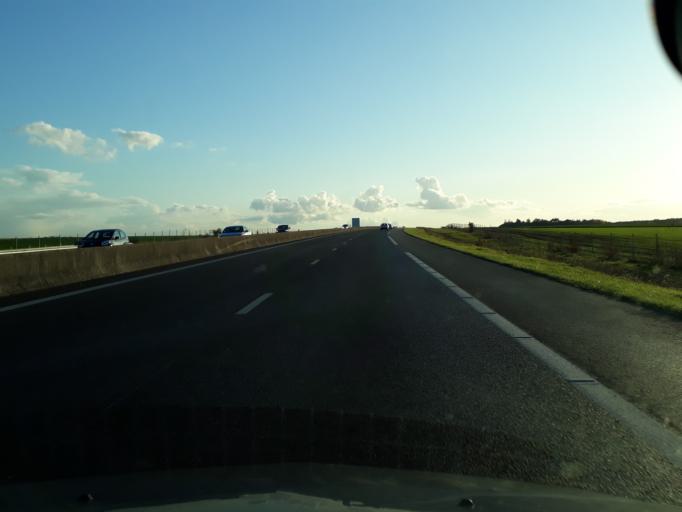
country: FR
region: Champagne-Ardenne
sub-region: Departement de l'Aube
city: Mailly-le-Camp
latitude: 48.7114
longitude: 4.2123
